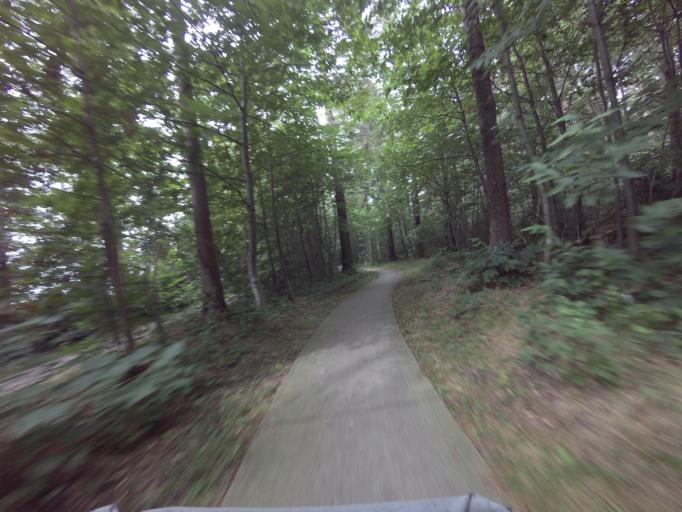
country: NL
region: Overijssel
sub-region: Gemeente Steenwijkerland
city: Tuk
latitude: 52.8254
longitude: 6.0961
